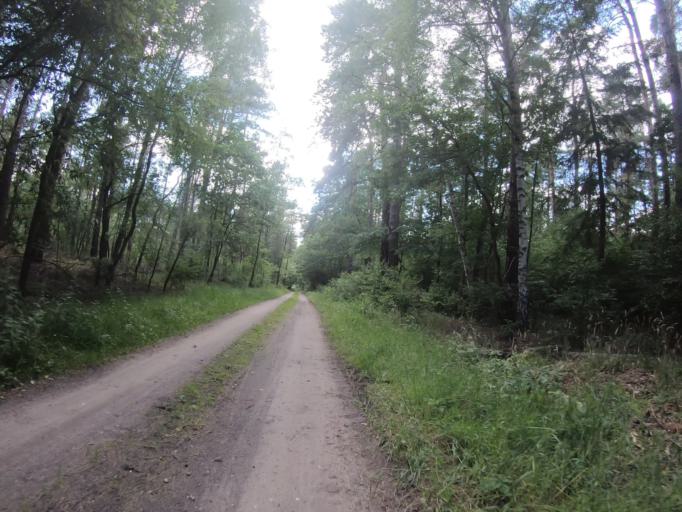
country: DE
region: Lower Saxony
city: Leiferde
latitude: 52.5042
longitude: 10.4449
